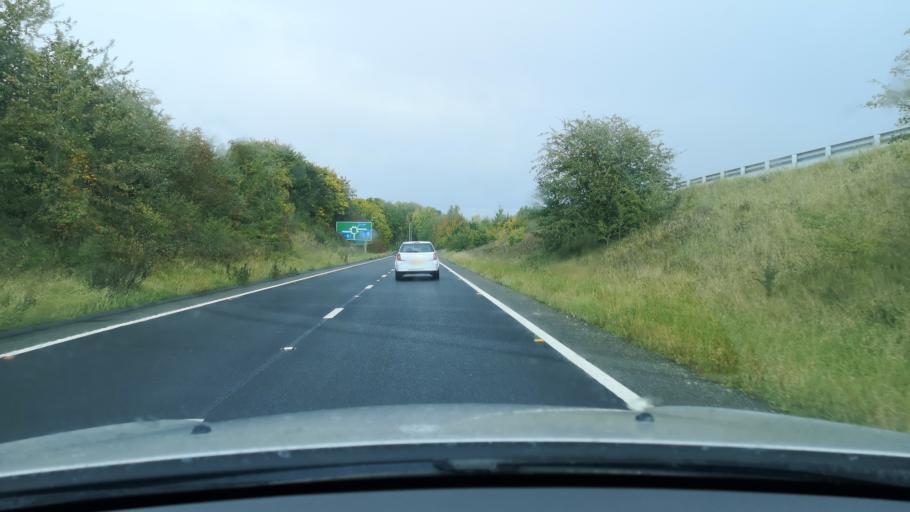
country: GB
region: England
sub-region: City and Borough of Wakefield
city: Darrington
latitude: 53.6917
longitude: -1.2669
